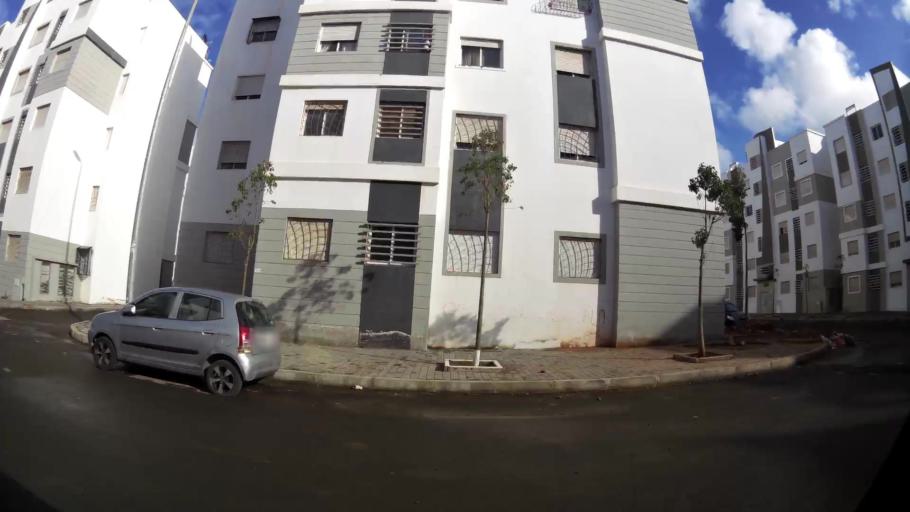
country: MA
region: Grand Casablanca
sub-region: Casablanca
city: Casablanca
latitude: 33.5539
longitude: -7.7051
